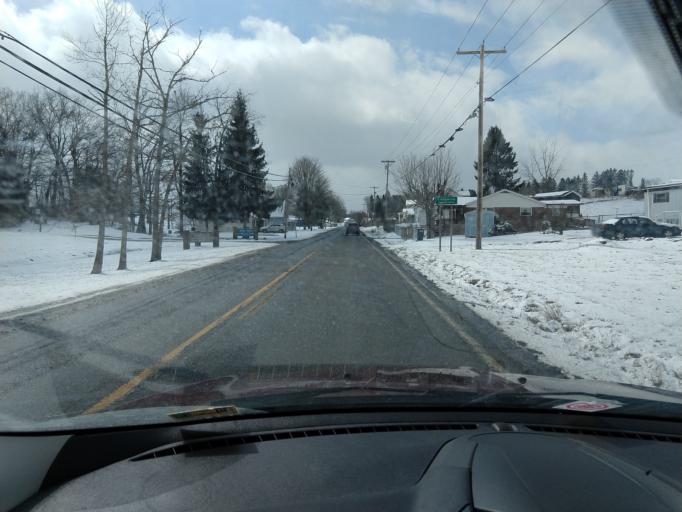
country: US
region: West Virginia
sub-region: Nicholas County
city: Craigsville
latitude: 38.3336
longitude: -80.6416
